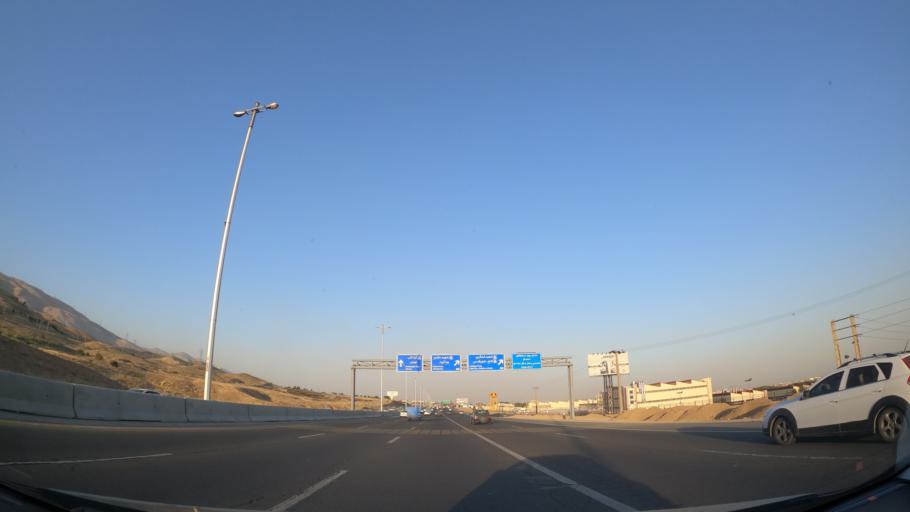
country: IR
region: Tehran
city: Shahr-e Qods
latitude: 35.7430
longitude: 51.1054
